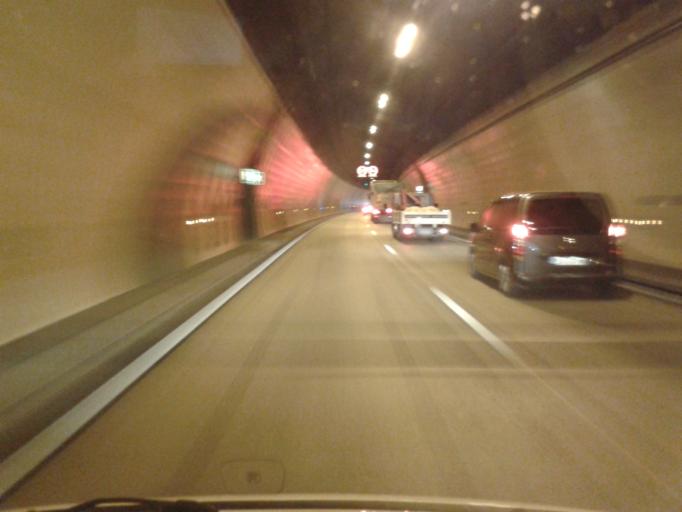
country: FR
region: Provence-Alpes-Cote d'Azur
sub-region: Departement des Alpes-Maritimes
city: Colomars
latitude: 43.7304
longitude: 7.2364
